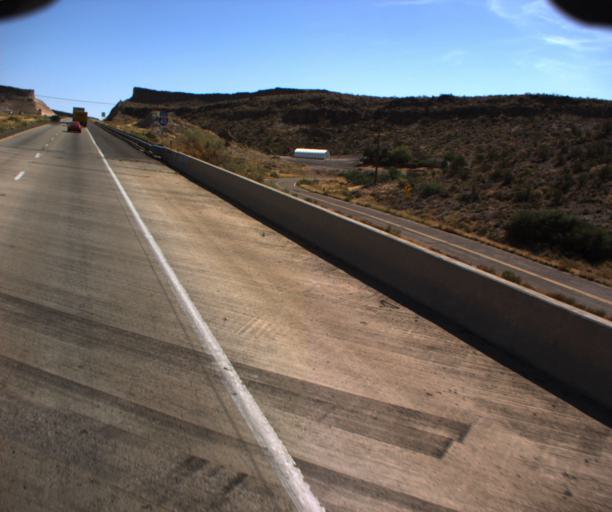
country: US
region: Arizona
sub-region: Mohave County
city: Kingman
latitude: 35.2029
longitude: -114.0638
